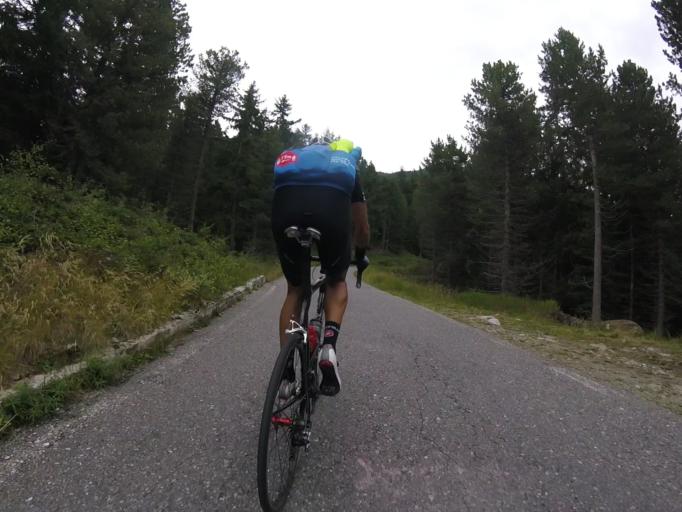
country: IT
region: Lombardy
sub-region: Provincia di Sondrio
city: Mazzo di Valtellina
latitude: 46.2464
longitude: 10.2887
